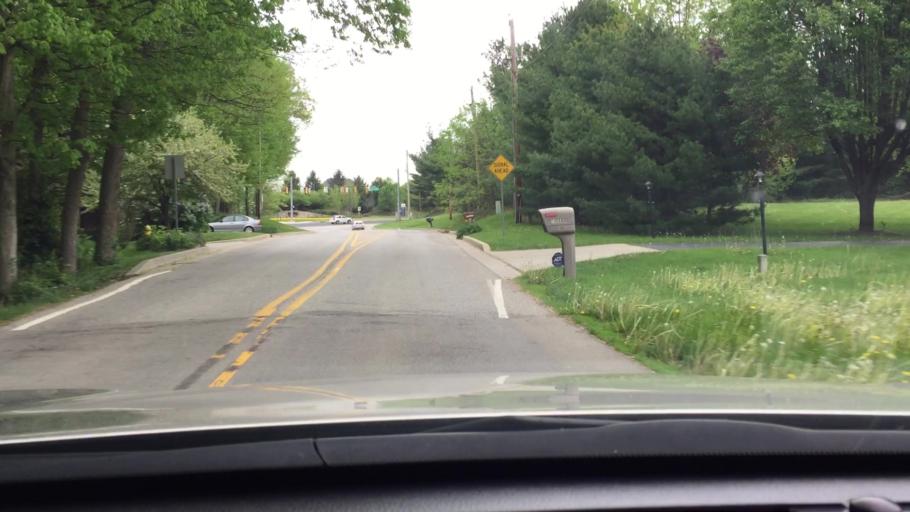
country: US
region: Indiana
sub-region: Hamilton County
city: Carmel
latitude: 39.9991
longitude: -86.0591
